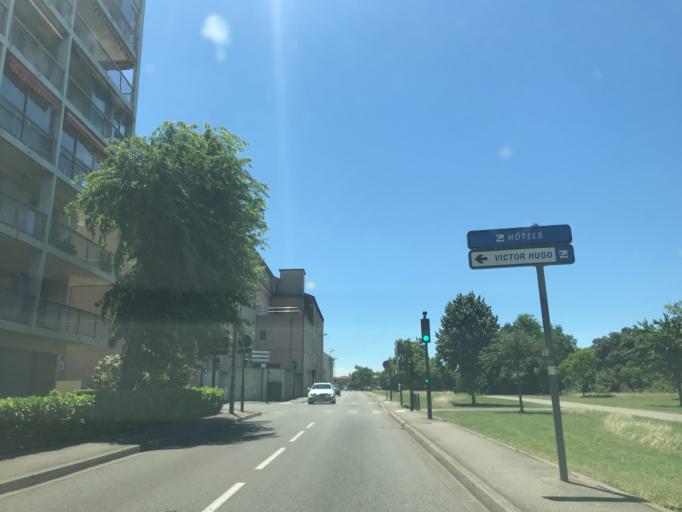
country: FR
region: Rhone-Alpes
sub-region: Departement de l'Ardeche
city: Guilherand-Granges
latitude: 44.9241
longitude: 4.8849
